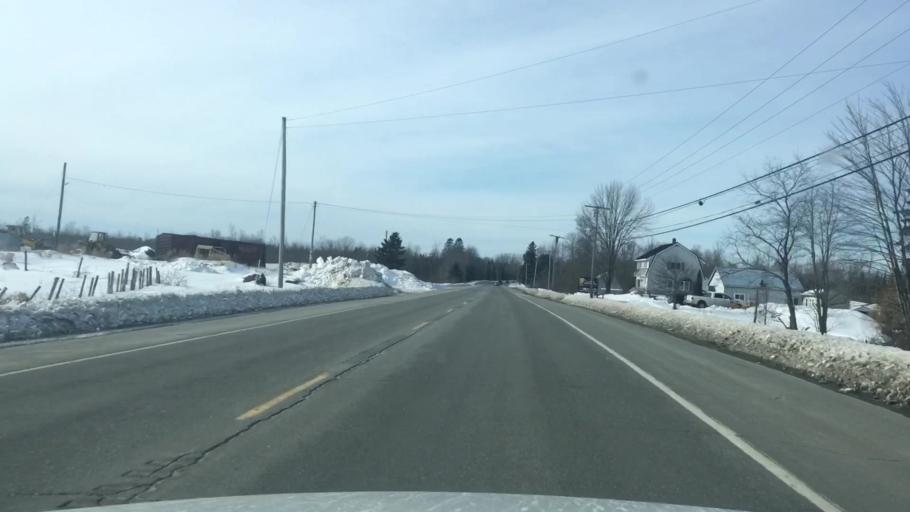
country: US
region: Maine
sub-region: Penobscot County
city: Kenduskeag
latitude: 44.9046
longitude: -68.8896
